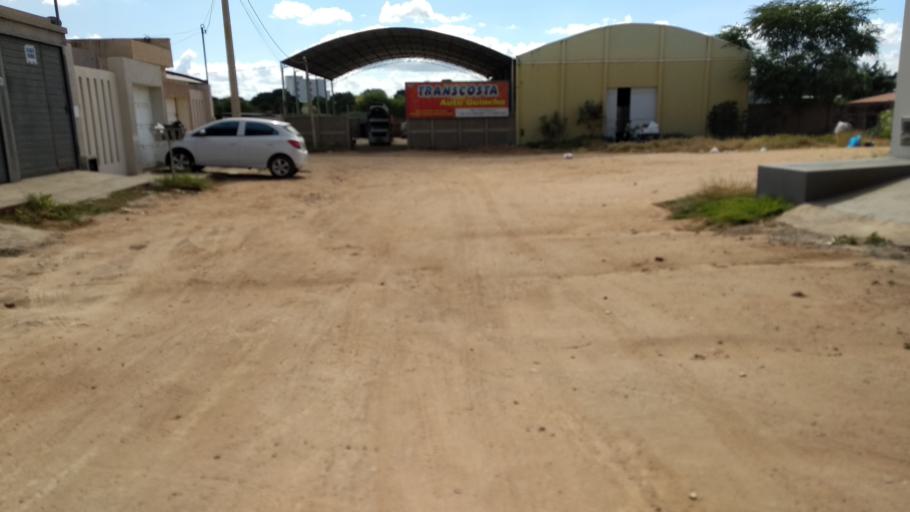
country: BR
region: Bahia
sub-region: Guanambi
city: Guanambi
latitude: -14.2393
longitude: -42.7712
